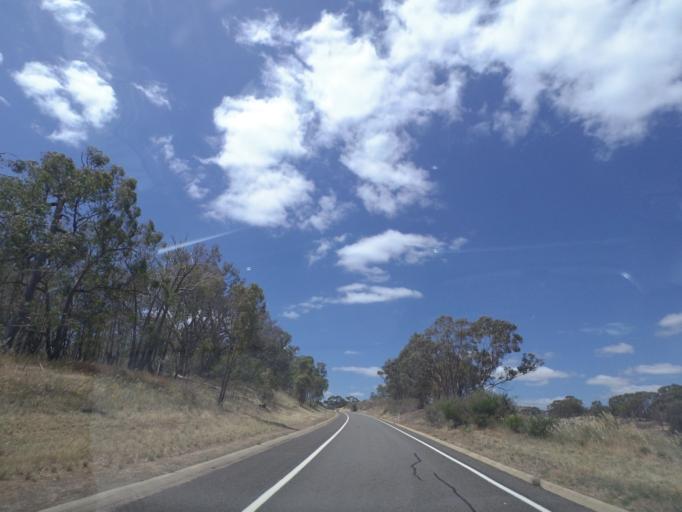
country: AU
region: Victoria
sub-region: Wangaratta
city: Wangaratta
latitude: -36.4684
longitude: 146.2071
